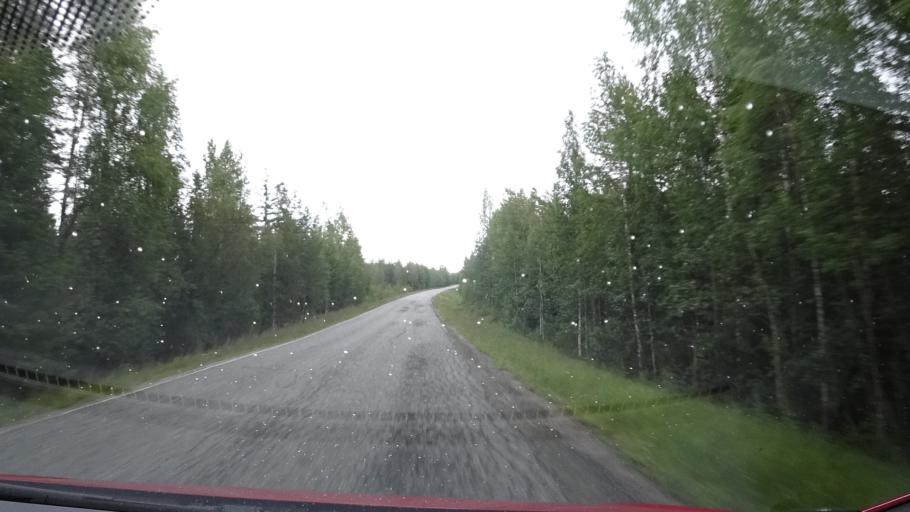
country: FI
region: Kainuu
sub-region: Kehys-Kainuu
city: Kuhmo
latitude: 63.9555
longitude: 29.2513
